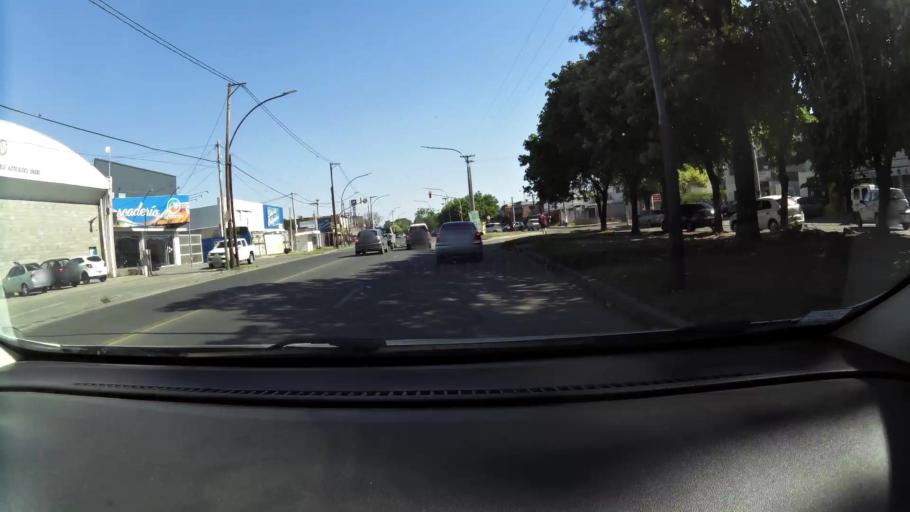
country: AR
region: Cordoba
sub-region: Departamento de Capital
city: Cordoba
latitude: -31.3695
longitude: -64.1761
